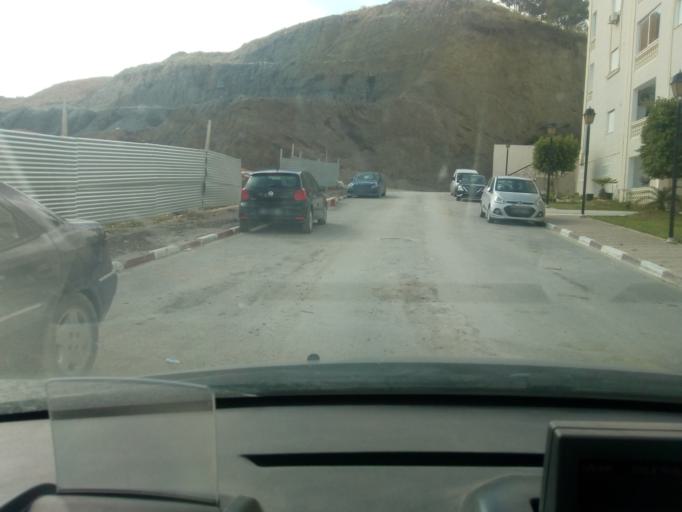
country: TN
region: Ariana
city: Ariana
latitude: 36.8763
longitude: 10.1796
